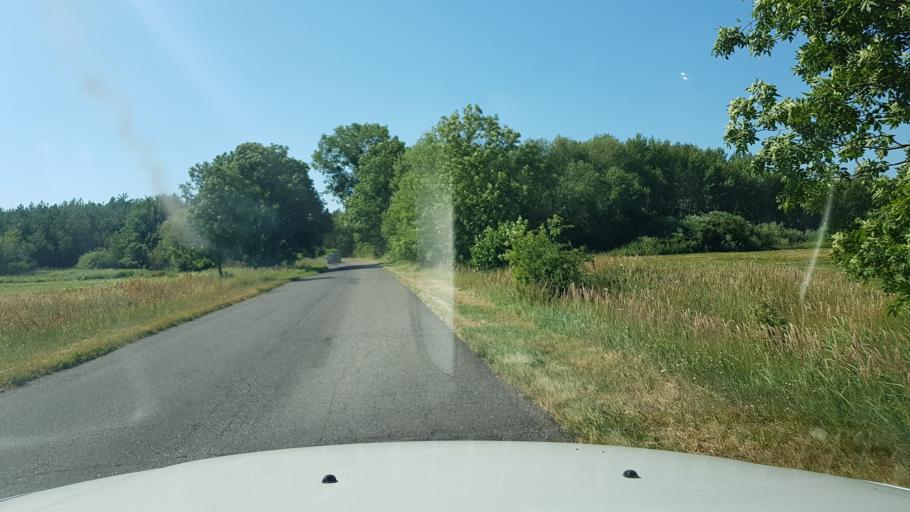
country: PL
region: West Pomeranian Voivodeship
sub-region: Powiat goleniowski
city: Goleniow
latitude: 53.4700
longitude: 14.7155
